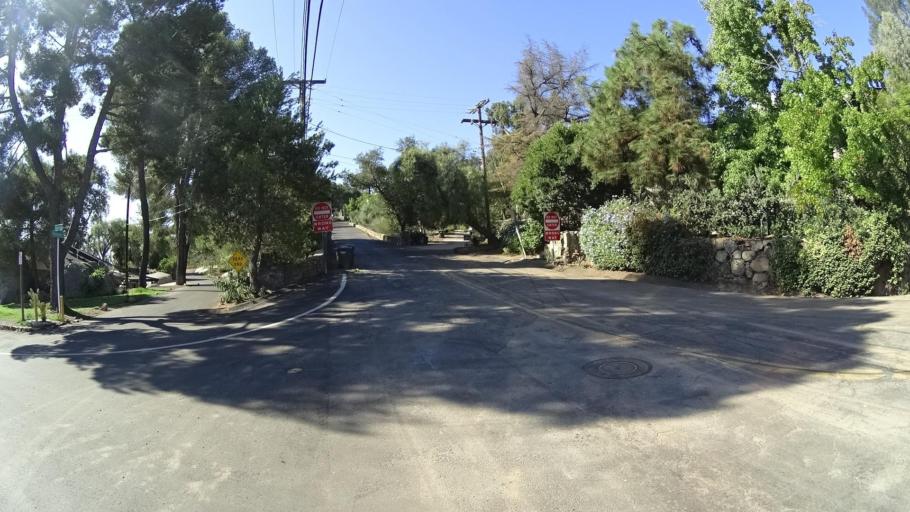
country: US
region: California
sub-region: San Diego County
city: Casa de Oro-Mount Helix
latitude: 32.7703
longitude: -116.9802
